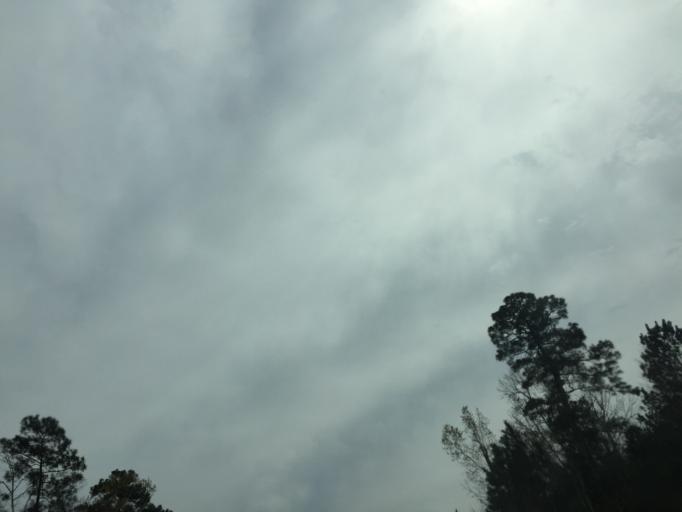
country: US
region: Georgia
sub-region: Chatham County
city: Pooler
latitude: 32.0655
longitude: -81.2442
